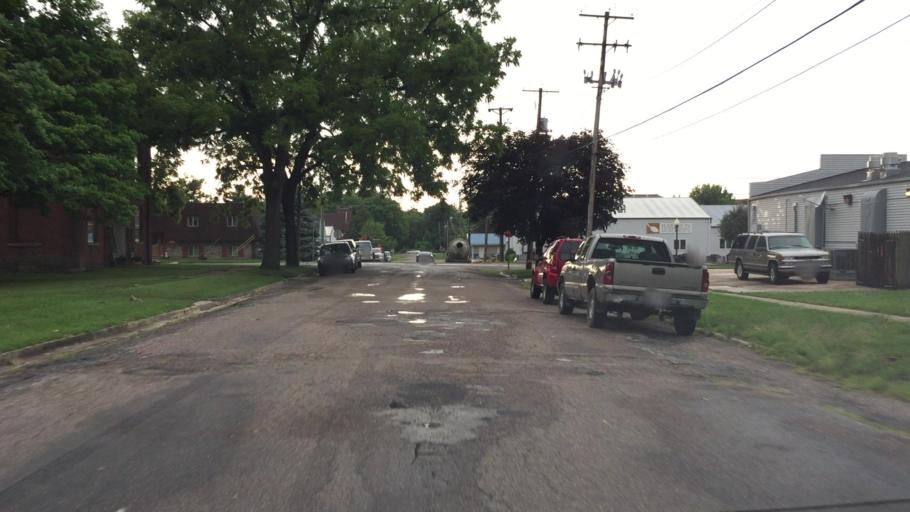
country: US
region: Illinois
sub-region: Hancock County
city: Warsaw
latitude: 40.3584
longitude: -91.4340
